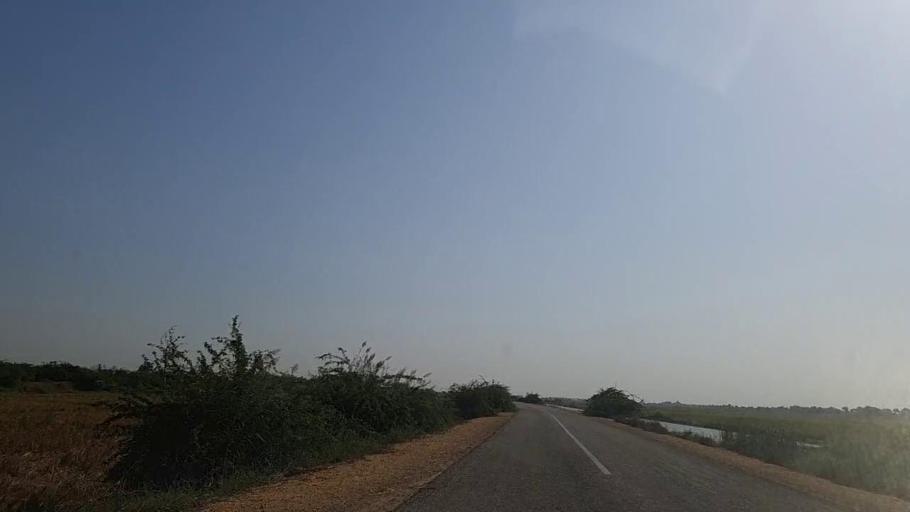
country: PK
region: Sindh
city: Jati
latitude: 24.5057
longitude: 68.2744
